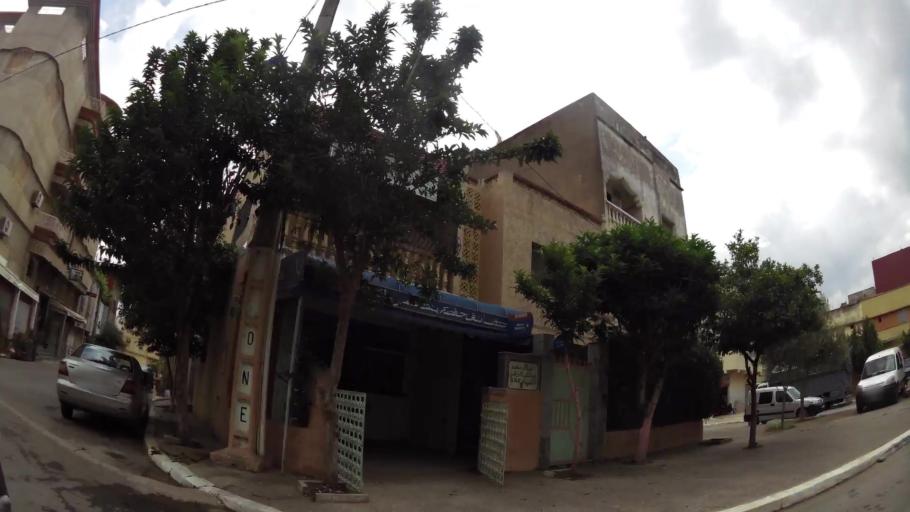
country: MA
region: Rabat-Sale-Zemmour-Zaer
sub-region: Khemisset
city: Tiflet
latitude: 33.8887
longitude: -6.3176
